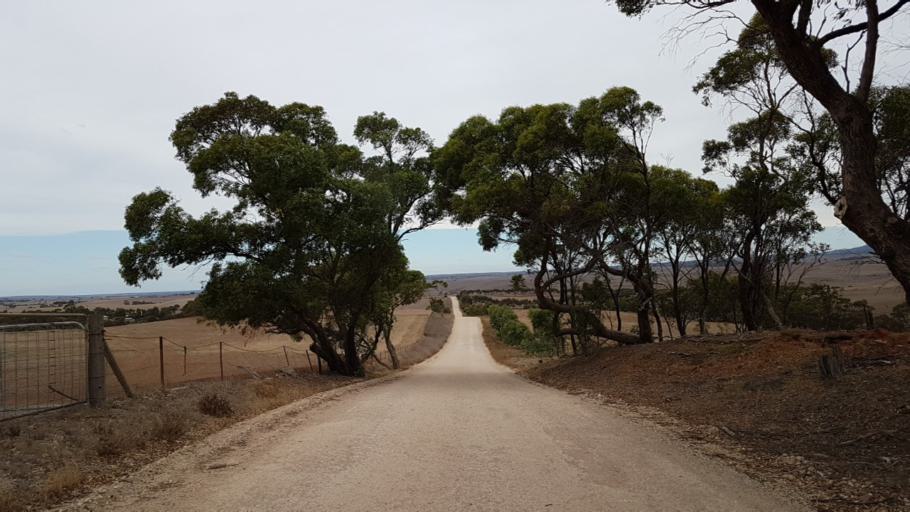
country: AU
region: South Australia
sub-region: Mount Barker
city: Callington
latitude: -35.0020
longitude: 139.0491
